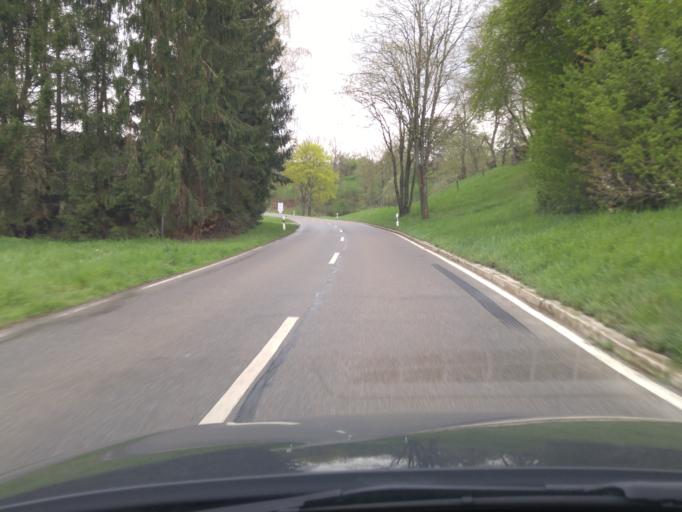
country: DE
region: Baden-Wuerttemberg
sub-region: Karlsruhe Region
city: Huffenhardt
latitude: 49.2876
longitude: 9.0700
